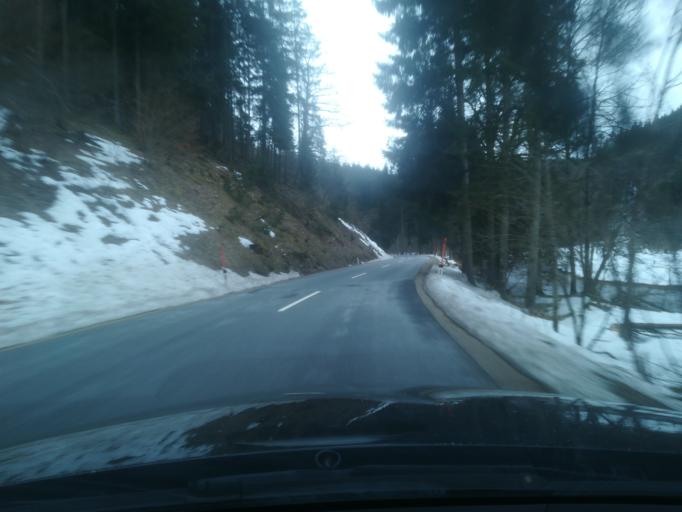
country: AT
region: Upper Austria
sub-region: Politischer Bezirk Perg
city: Perg
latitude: 48.3980
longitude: 14.6381
